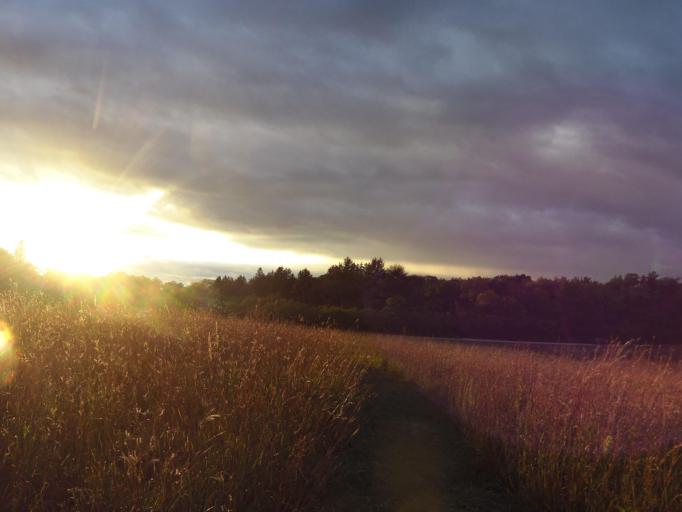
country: US
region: Minnesota
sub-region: Washington County
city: Lake Saint Croix Beach
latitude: 44.9371
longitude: -92.7954
